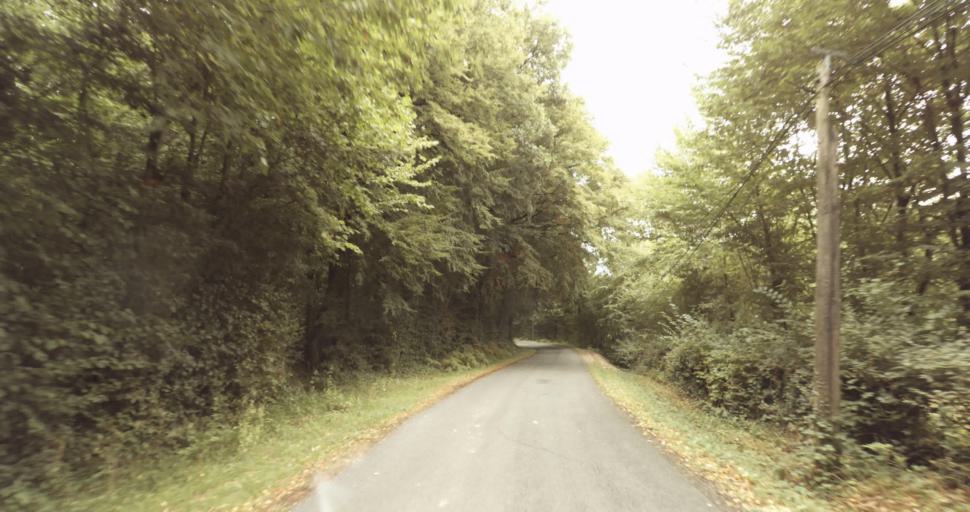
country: FR
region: Lower Normandy
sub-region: Departement de l'Orne
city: Gace
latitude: 48.8284
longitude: 0.2664
